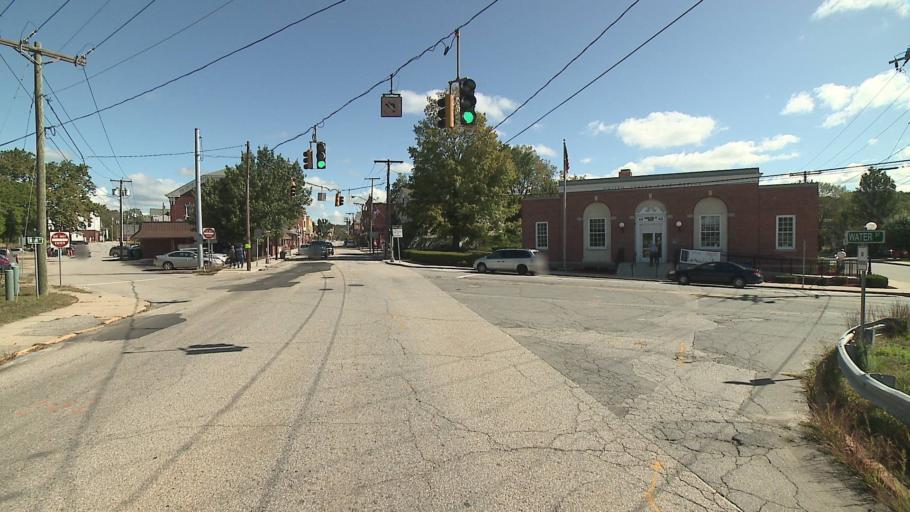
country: US
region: Connecticut
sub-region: Windham County
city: Danielson
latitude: 41.8032
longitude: -71.8859
